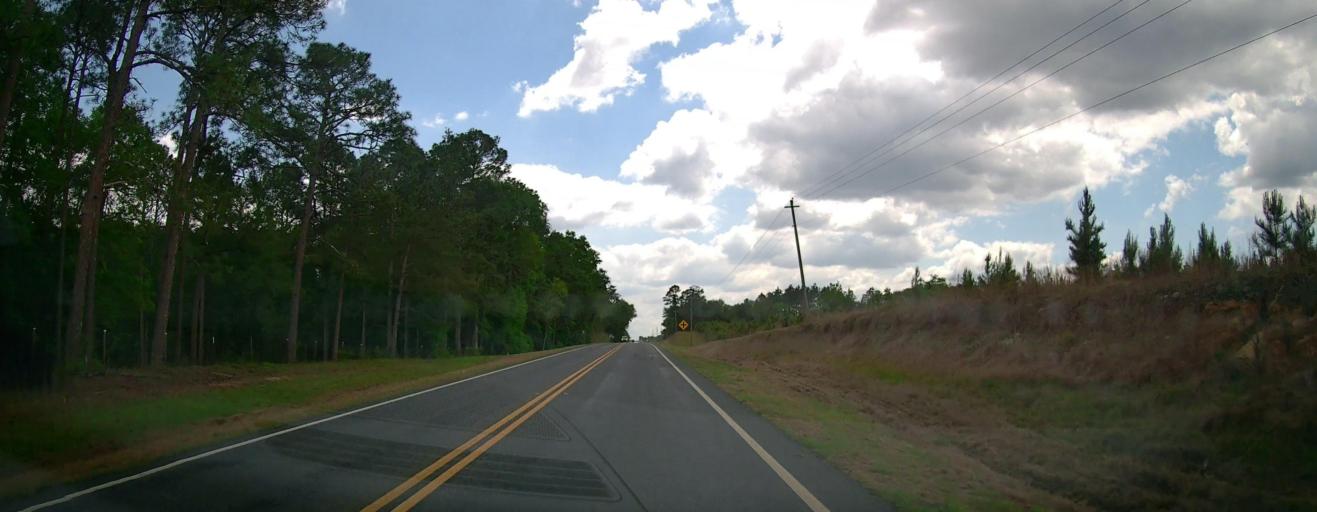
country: US
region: Georgia
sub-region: Treutlen County
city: Soperton
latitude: 32.4475
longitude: -82.6057
